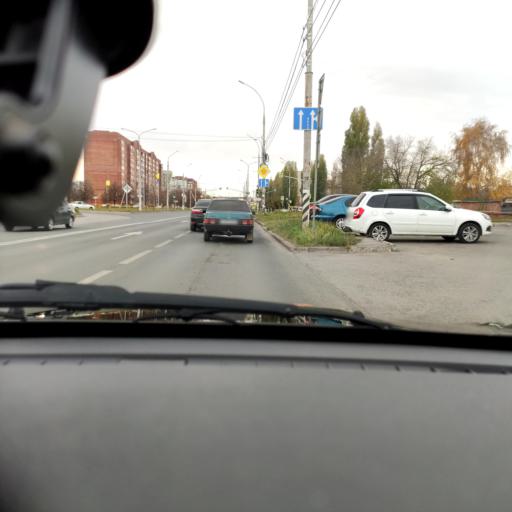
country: RU
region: Samara
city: Tol'yatti
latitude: 53.5437
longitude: 49.3161
